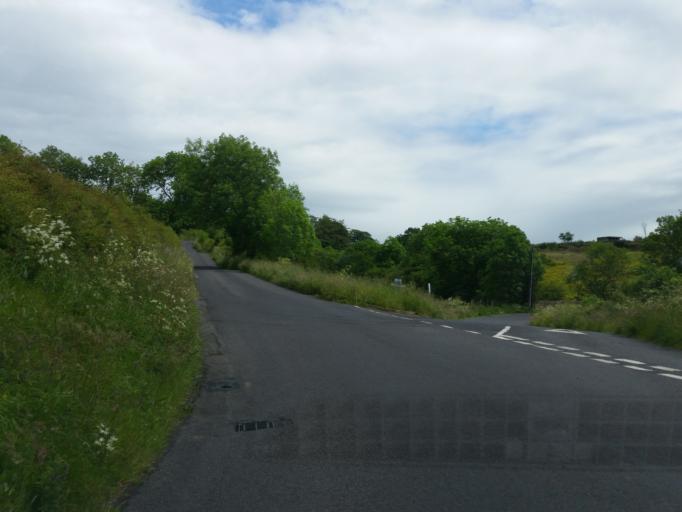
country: GB
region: Northern Ireland
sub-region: Omagh District
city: Omagh
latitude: 54.5486
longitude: -7.0903
